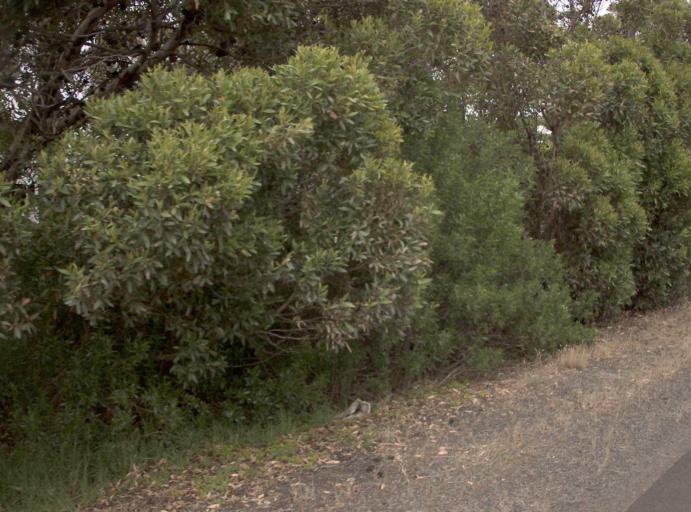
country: AU
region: Victoria
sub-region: Bass Coast
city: Phillip Island
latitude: -38.5202
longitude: 145.3396
